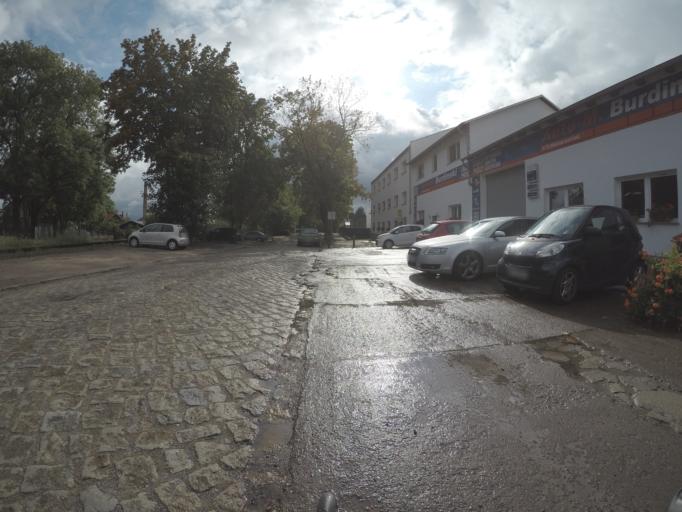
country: DE
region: Berlin
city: Blankenfelde
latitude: 52.6410
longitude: 13.3739
